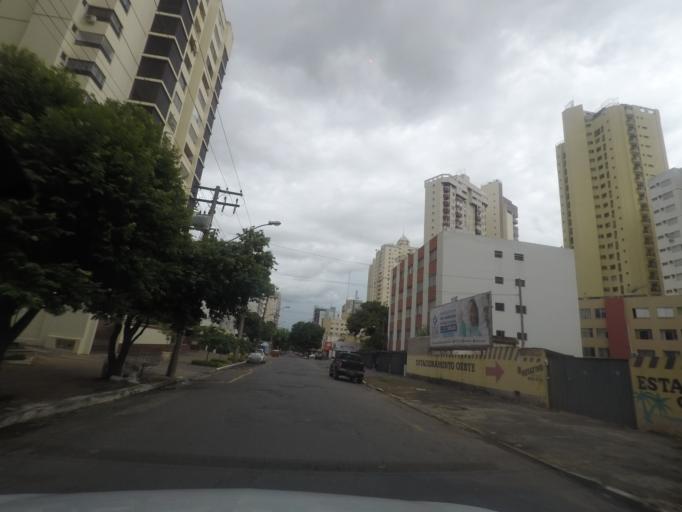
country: BR
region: Goias
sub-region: Goiania
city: Goiania
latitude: -16.6821
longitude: -49.2642
